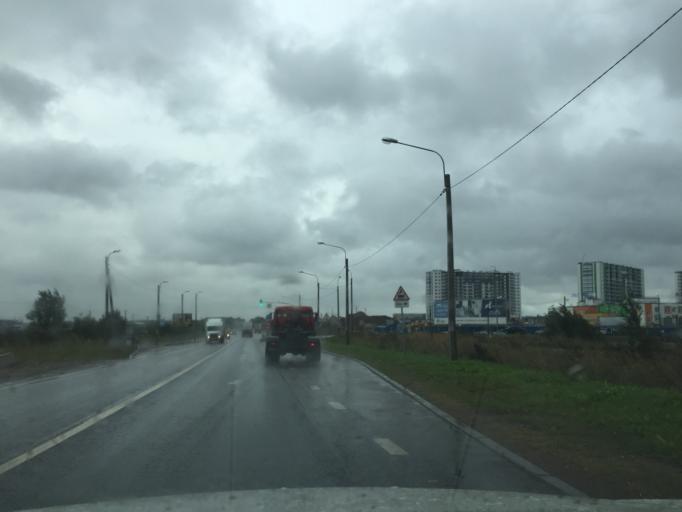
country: RU
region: St.-Petersburg
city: Uritsk
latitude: 59.7955
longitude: 30.1670
